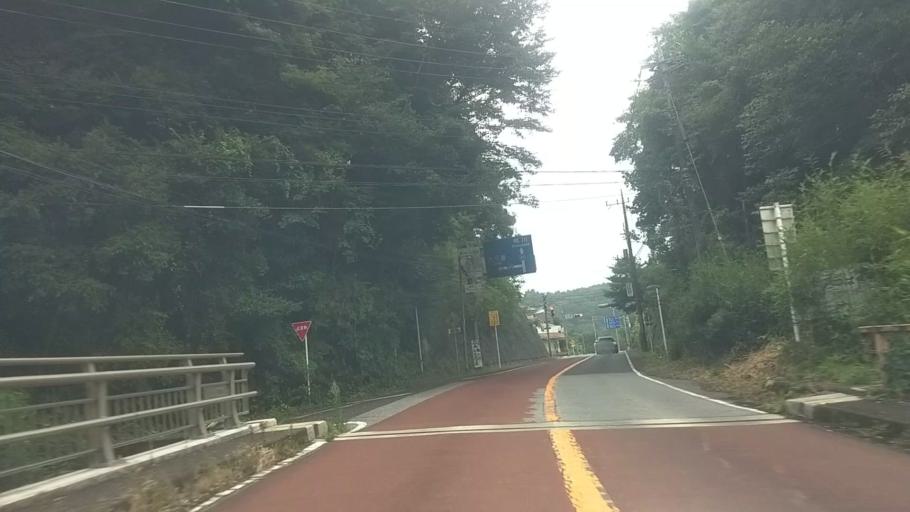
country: JP
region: Chiba
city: Kawaguchi
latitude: 35.2486
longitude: 140.0766
